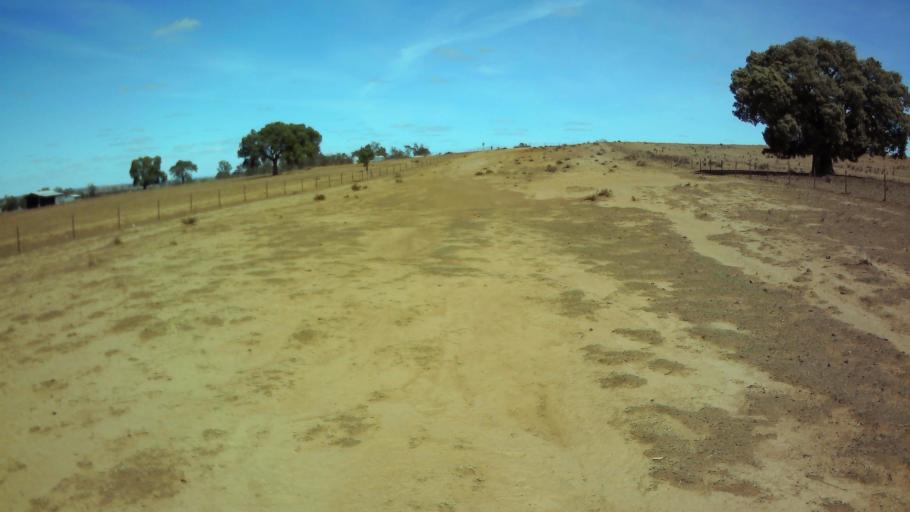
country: AU
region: New South Wales
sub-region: Forbes
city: Forbes
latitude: -33.7173
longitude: 147.8163
